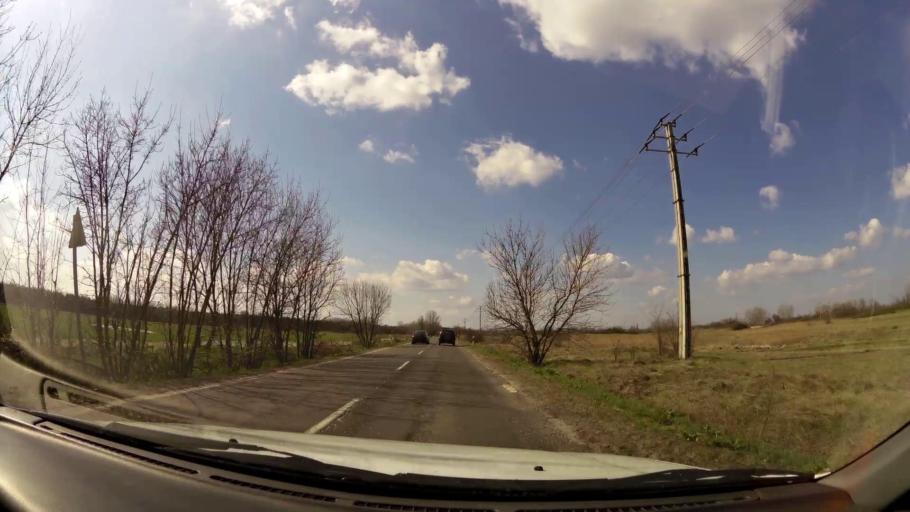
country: HU
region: Pest
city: Farmos
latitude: 47.3555
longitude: 19.8288
